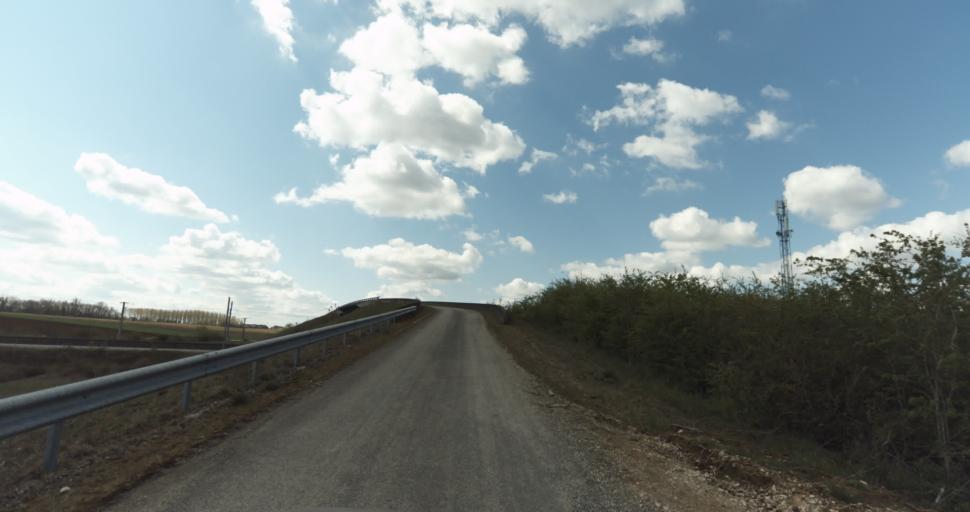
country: FR
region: Bourgogne
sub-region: Departement de la Cote-d'Or
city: Auxonne
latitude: 47.2239
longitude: 5.4258
